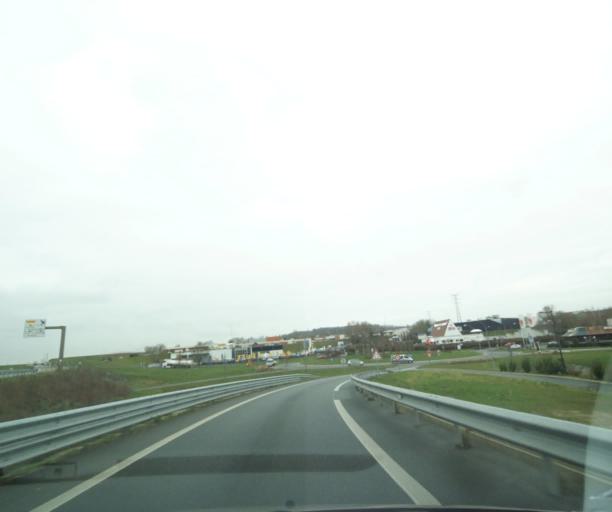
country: FR
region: Picardie
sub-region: Departement de l'Oise
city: Noyon
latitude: 49.5684
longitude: 2.9813
